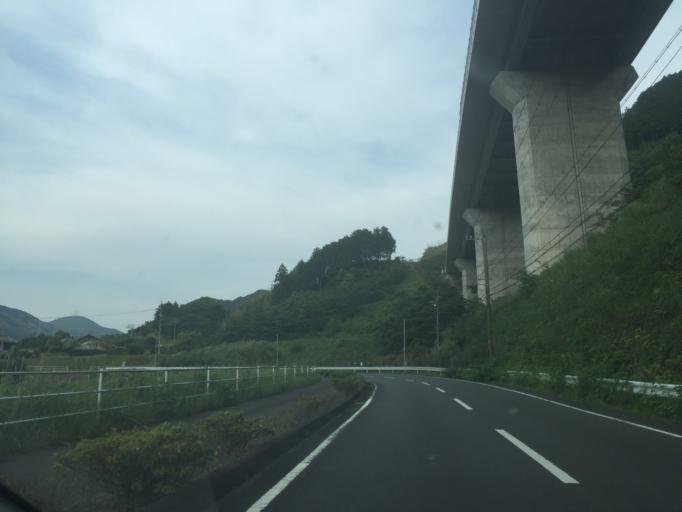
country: JP
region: Shizuoka
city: Mori
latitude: 34.8445
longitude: 138.0031
